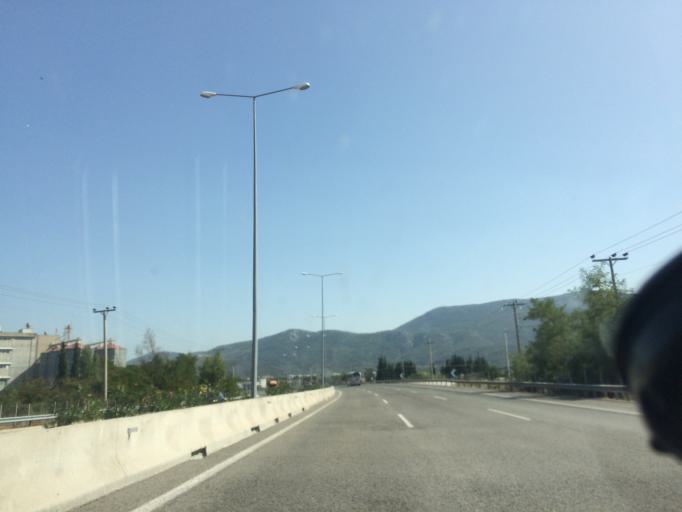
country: GR
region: Attica
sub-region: Nomarchia Anatolikis Attikis
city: Avlonas
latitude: 38.2728
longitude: 23.6936
